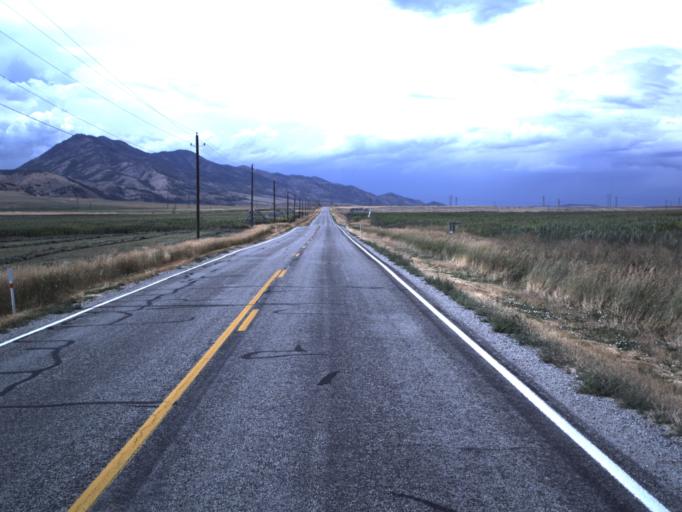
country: US
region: Utah
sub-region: Cache County
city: Benson
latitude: 41.8682
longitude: -112.0107
